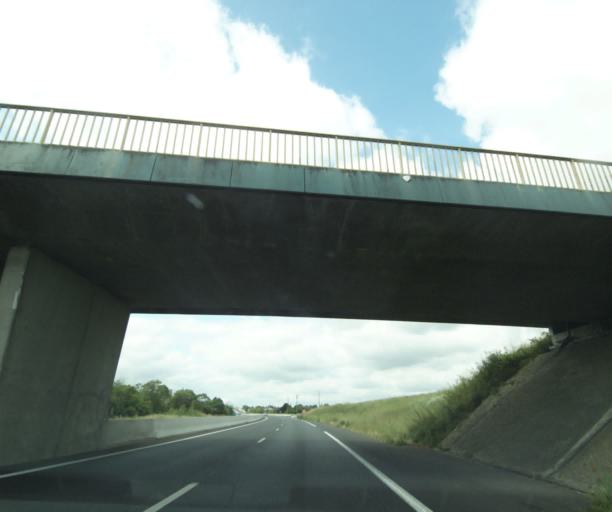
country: FR
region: Pays de la Loire
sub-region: Departement de Maine-et-Loire
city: Saumur
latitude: 47.2807
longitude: -0.0685
